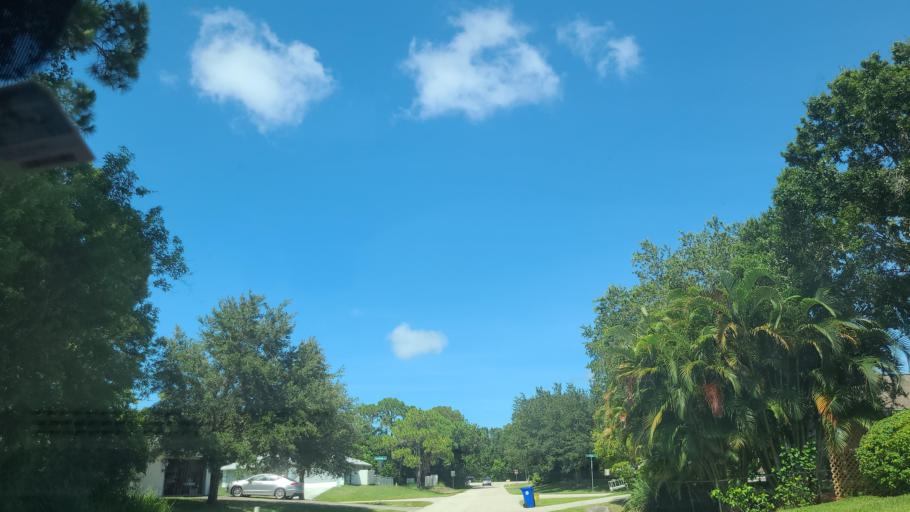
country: US
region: Florida
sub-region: Indian River County
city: Sebastian
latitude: 27.7721
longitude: -80.4840
